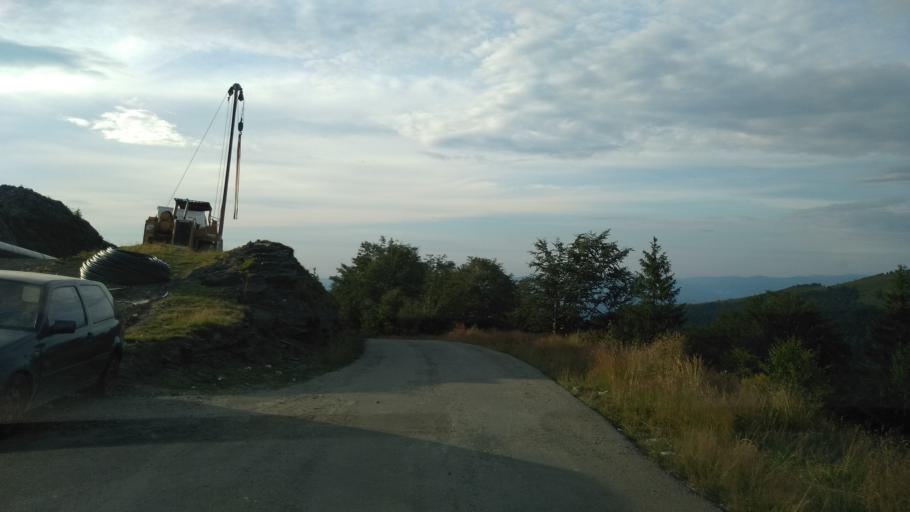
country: RO
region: Hunedoara
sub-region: Municipiul  Vulcan
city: Jiu-Paroseni
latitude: 45.3170
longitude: 23.3037
